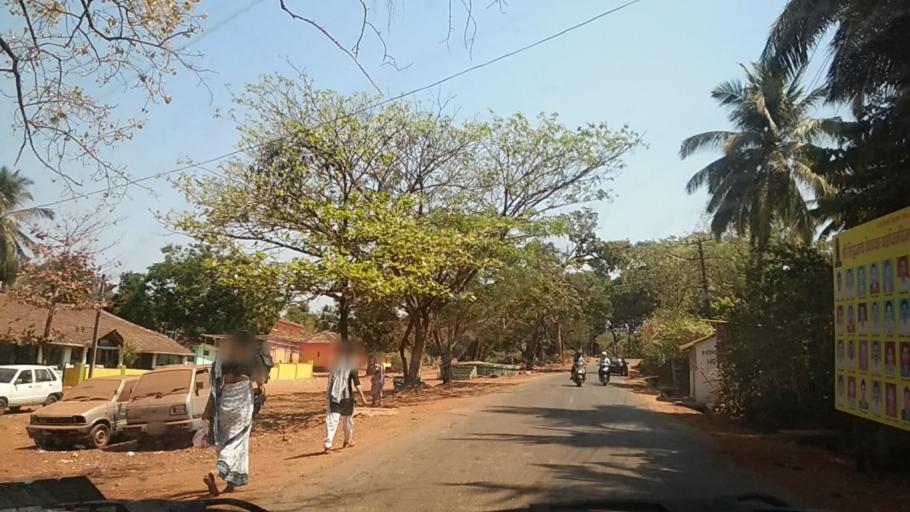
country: IN
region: Goa
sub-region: North Goa
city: Dicholi
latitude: 15.5826
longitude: 73.9300
